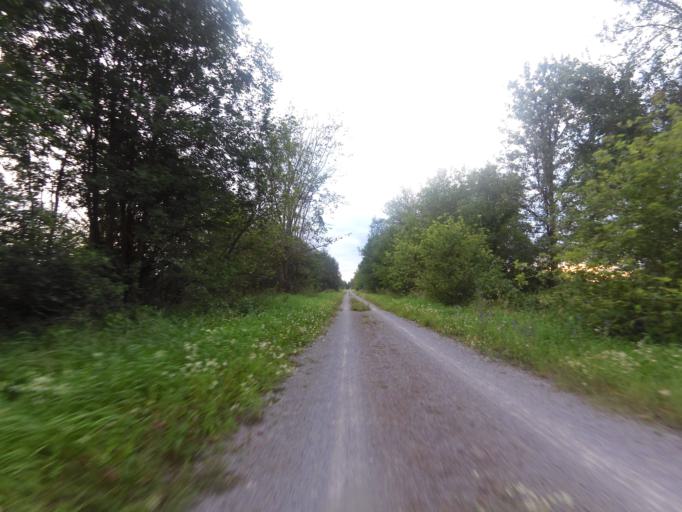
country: CA
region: Ontario
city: Carleton Place
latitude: 45.1552
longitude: -76.0921
